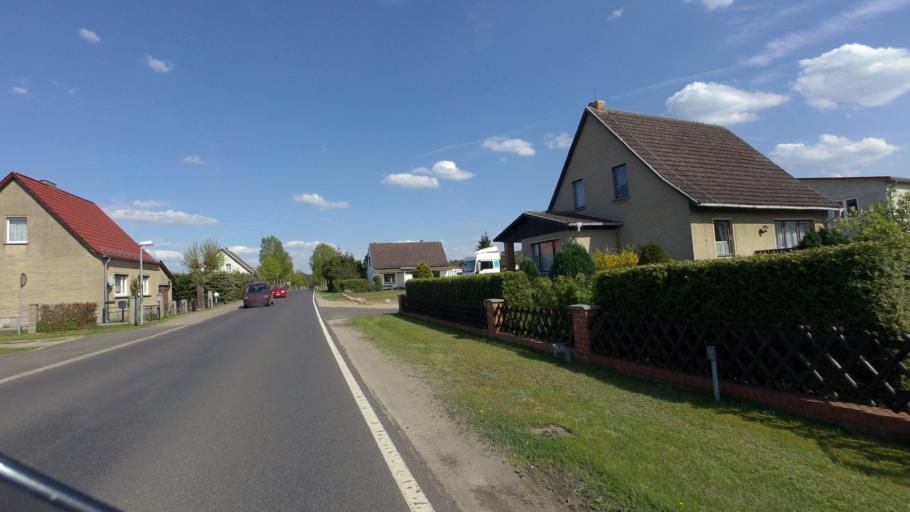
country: DE
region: Brandenburg
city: Templin
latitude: 53.0509
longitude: 13.5343
